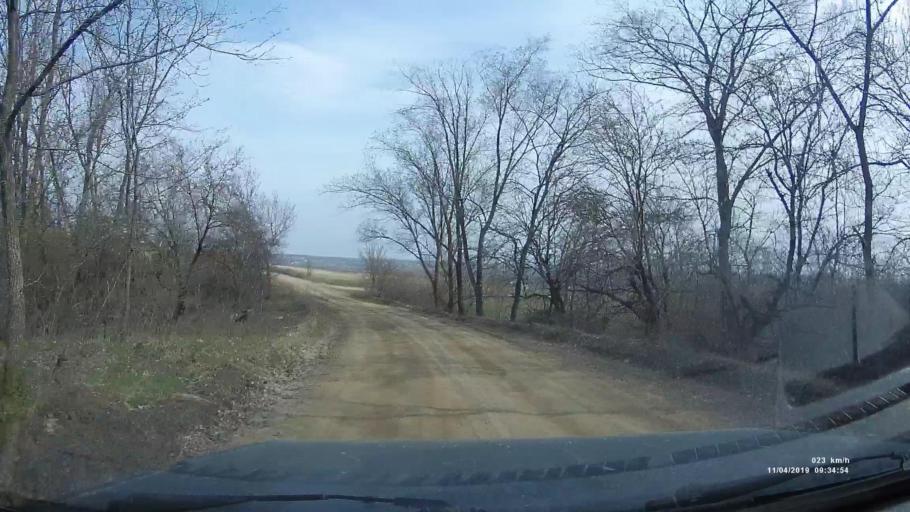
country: RU
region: Rostov
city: Staraya Stanitsa
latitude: 48.2703
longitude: 40.3715
